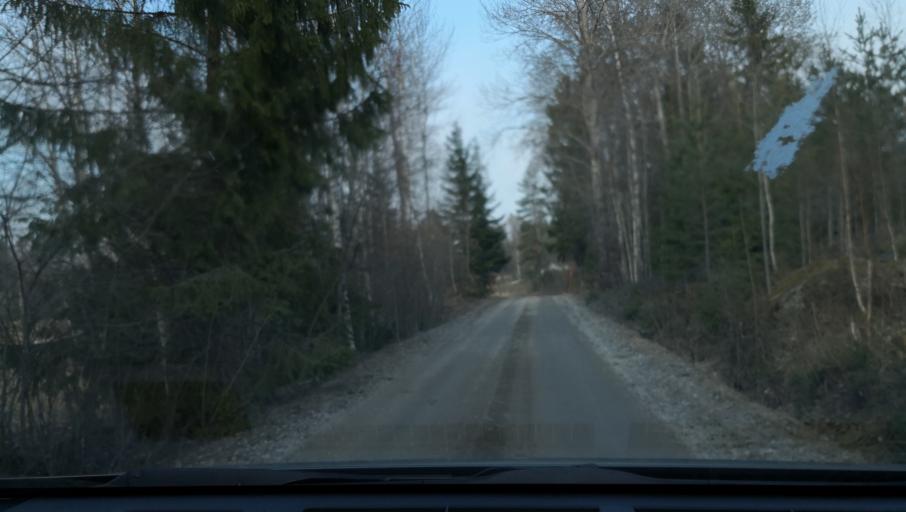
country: SE
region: OErebro
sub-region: Lindesbergs Kommun
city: Frovi
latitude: 59.3851
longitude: 15.3614
